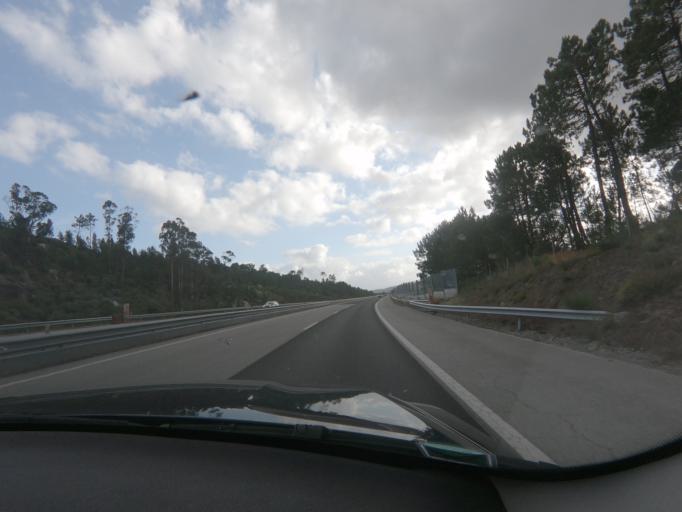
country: PT
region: Viseu
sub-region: Castro Daire
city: Castro Daire
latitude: 40.8753
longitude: -7.9217
